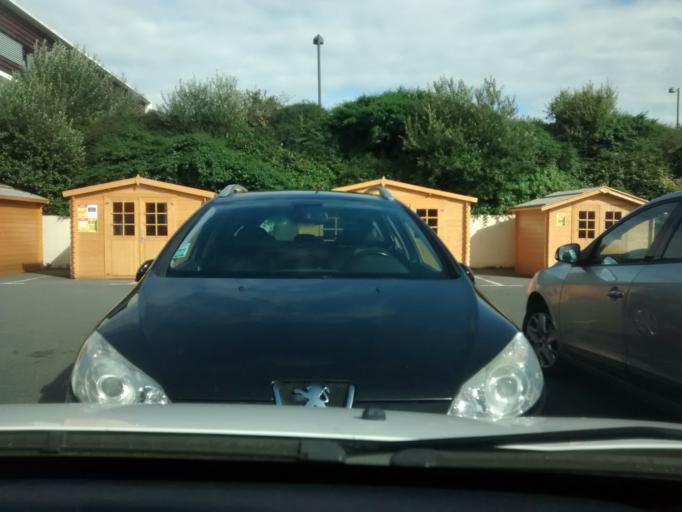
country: FR
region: Brittany
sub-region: Departement des Cotes-d'Armor
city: Lannion
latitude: 48.7333
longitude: -3.4387
